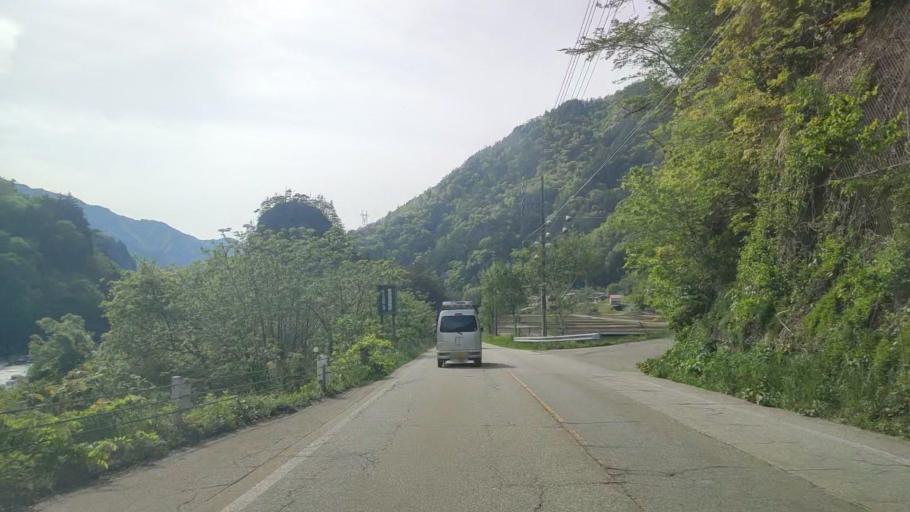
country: JP
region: Gifu
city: Takayama
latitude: 36.2667
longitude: 137.4250
